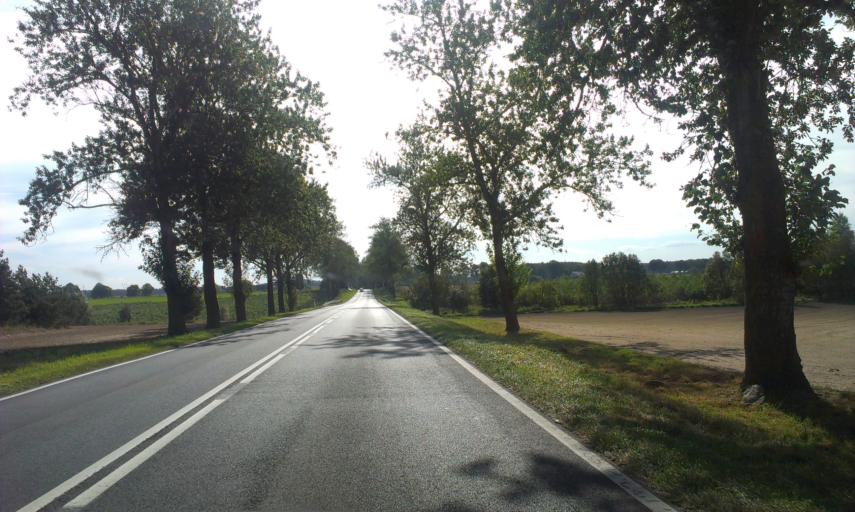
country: PL
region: Greater Poland Voivodeship
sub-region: Powiat zlotowski
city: Okonek
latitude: 53.5734
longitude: 16.8272
